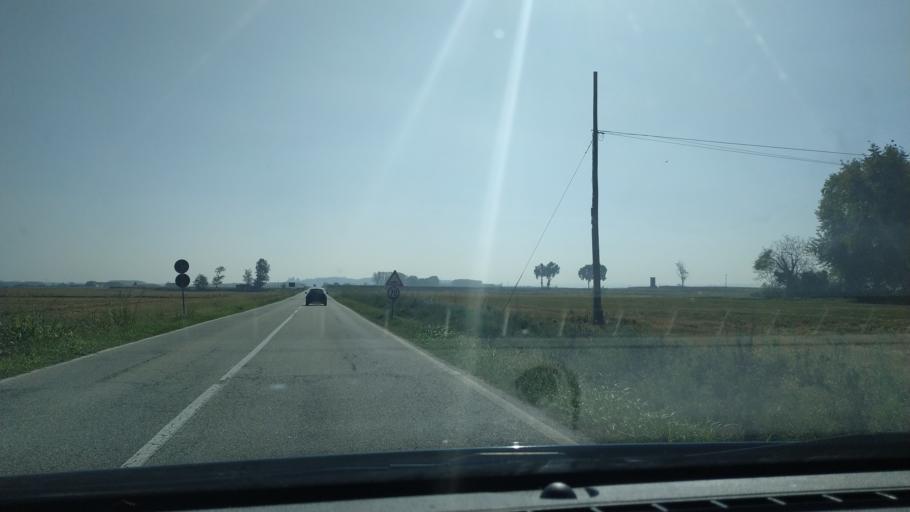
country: IT
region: Piedmont
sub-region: Provincia di Alessandria
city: Ticineto
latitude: 45.0866
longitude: 8.5527
